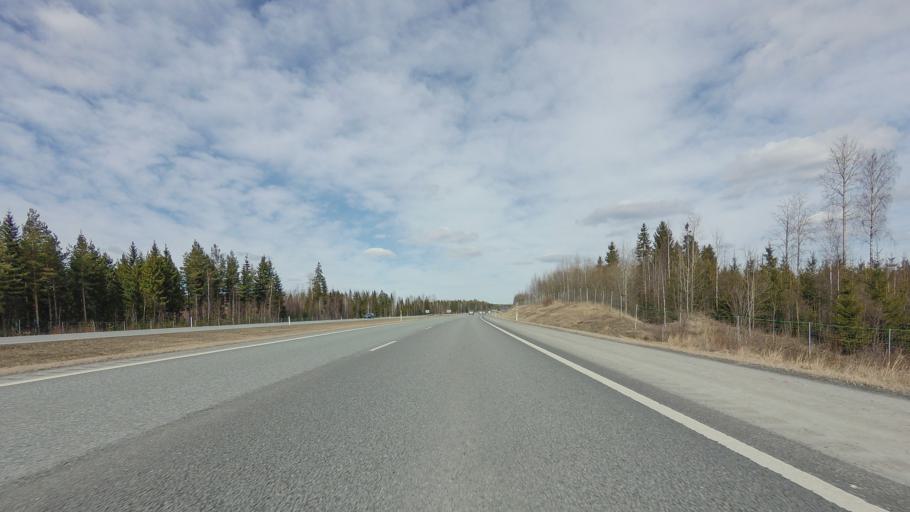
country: FI
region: Pirkanmaa
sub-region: Tampere
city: Lempaeaelae
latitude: 61.2847
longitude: 23.8100
